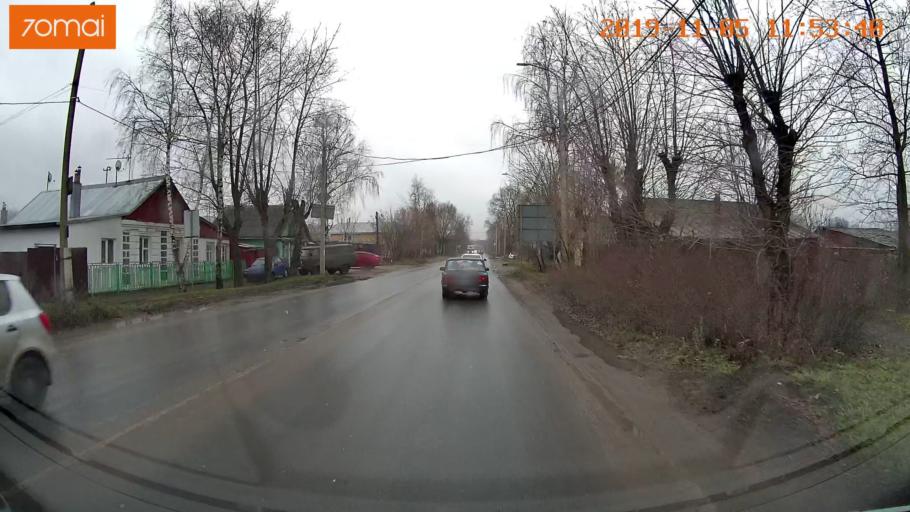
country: RU
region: Ivanovo
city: Bogorodskoye
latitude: 56.9951
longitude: 41.0305
